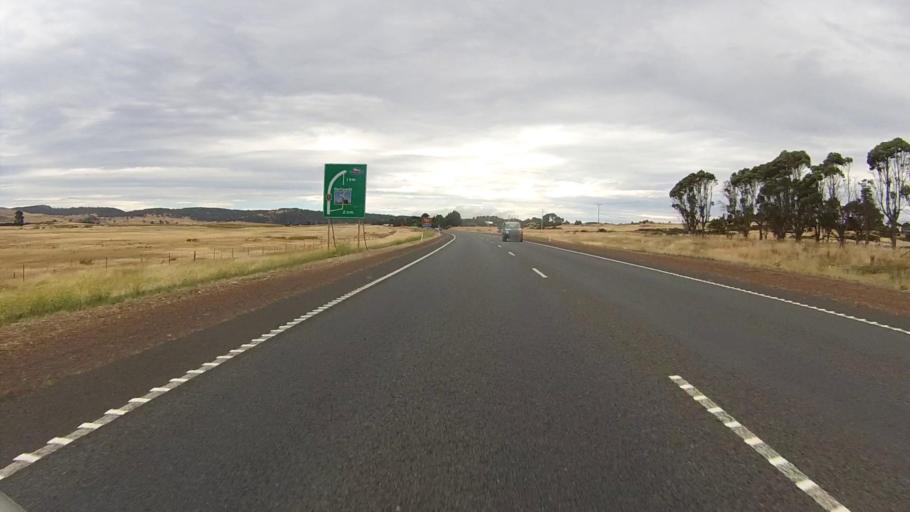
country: AU
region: Tasmania
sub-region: Brighton
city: Bridgewater
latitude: -42.3176
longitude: 147.3521
